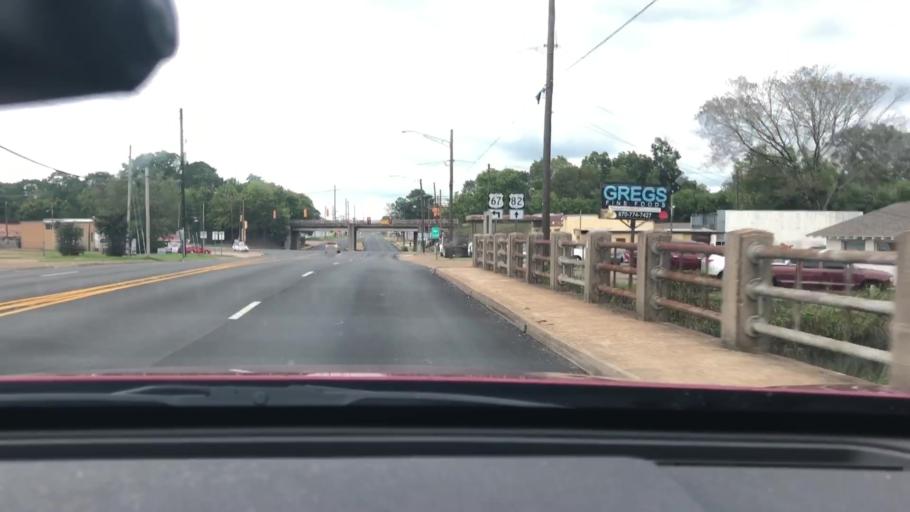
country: US
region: Arkansas
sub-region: Miller County
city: Texarkana
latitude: 33.4308
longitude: -94.0293
